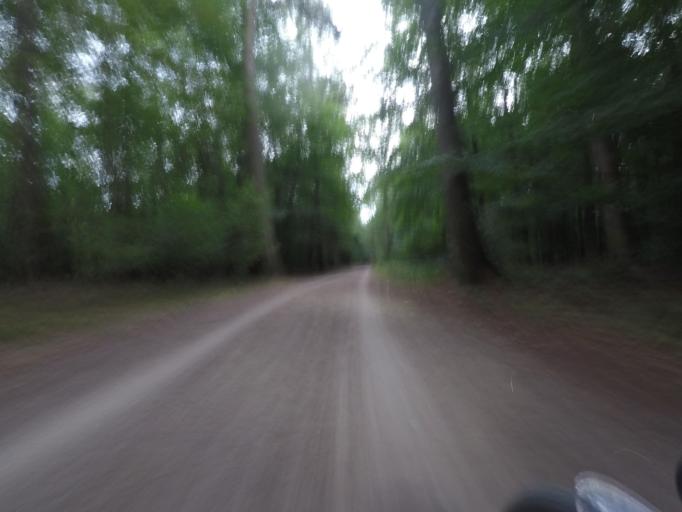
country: DE
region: Hamburg
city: Sasel
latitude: 53.6460
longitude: 10.1373
